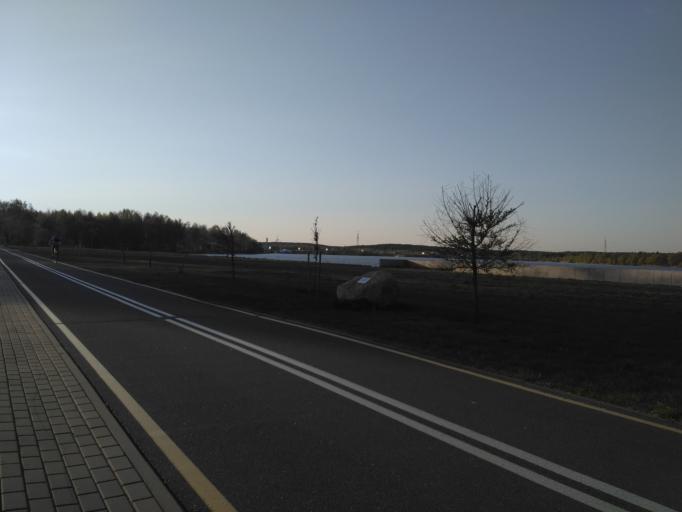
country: BY
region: Minsk
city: Zhdanovichy
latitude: 53.9447
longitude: 27.4619
